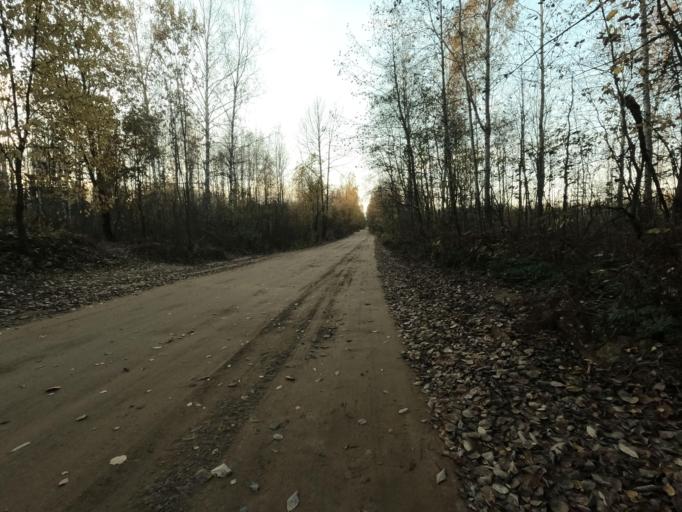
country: RU
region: Leningrad
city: Mga
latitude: 59.7582
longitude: 31.2694
